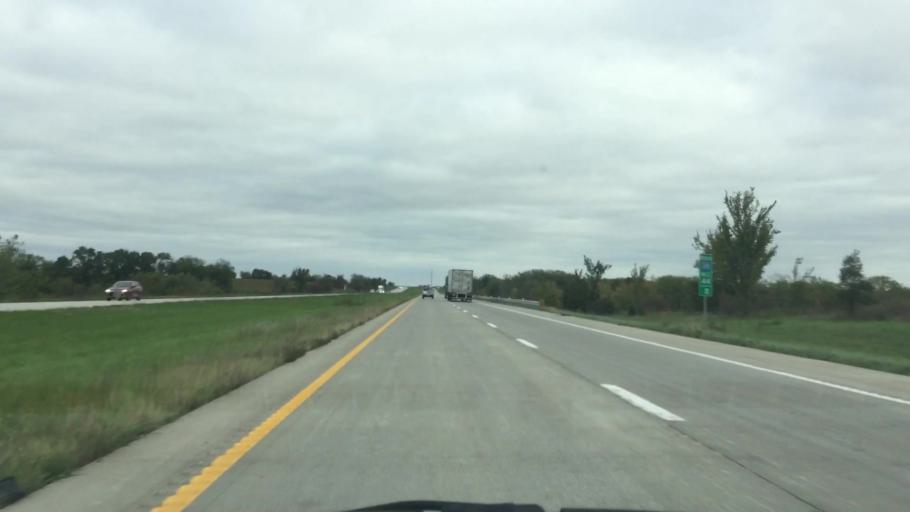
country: US
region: Missouri
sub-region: Clinton County
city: Lathrop
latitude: 39.6190
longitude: -94.2482
